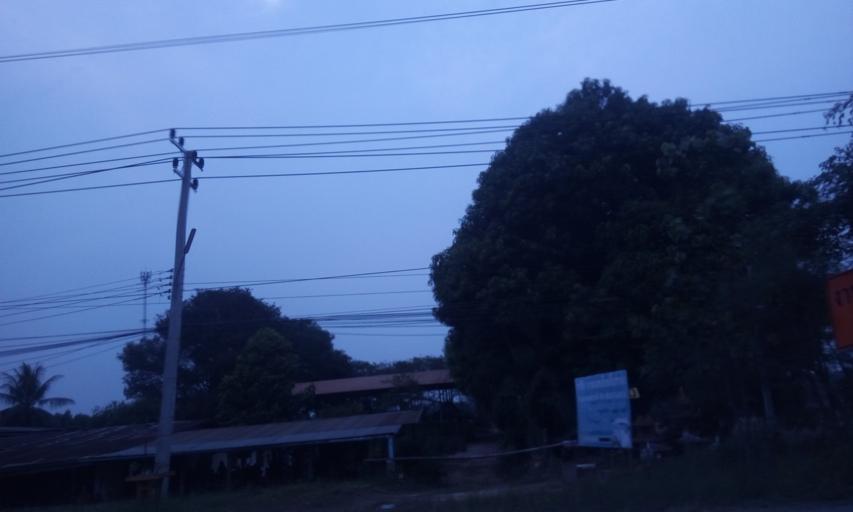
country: TH
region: Chon Buri
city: Ko Chan
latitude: 13.4615
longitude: 101.2840
